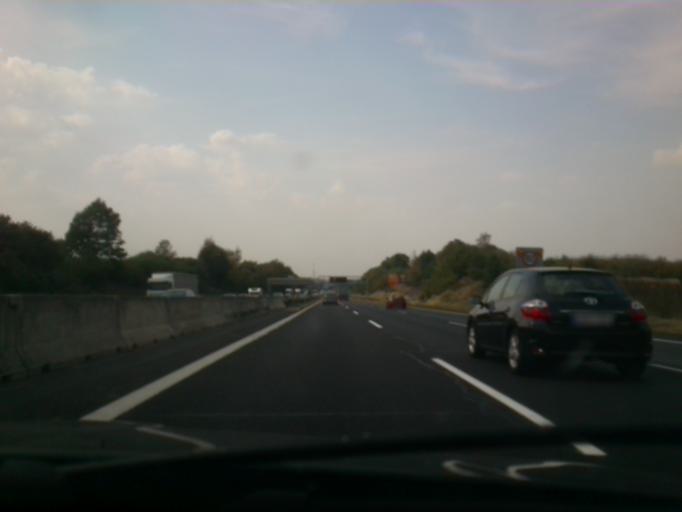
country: CZ
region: Central Bohemia
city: Velke Popovice
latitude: 49.9499
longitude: 14.6439
